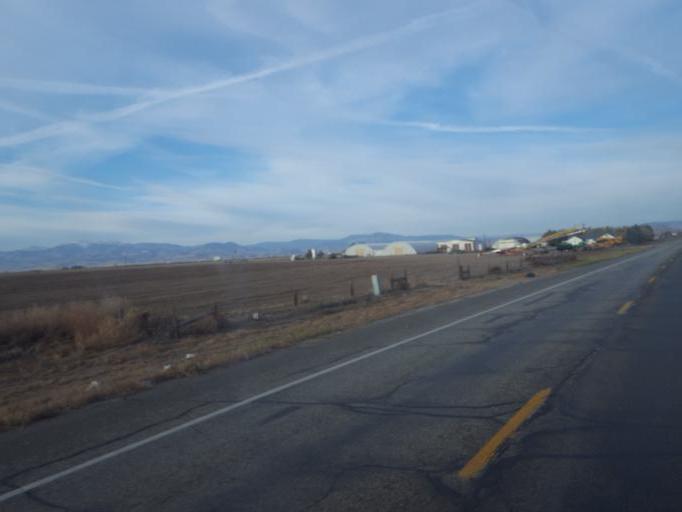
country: US
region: Colorado
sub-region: Saguache County
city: Center
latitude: 37.7482
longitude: -106.1260
